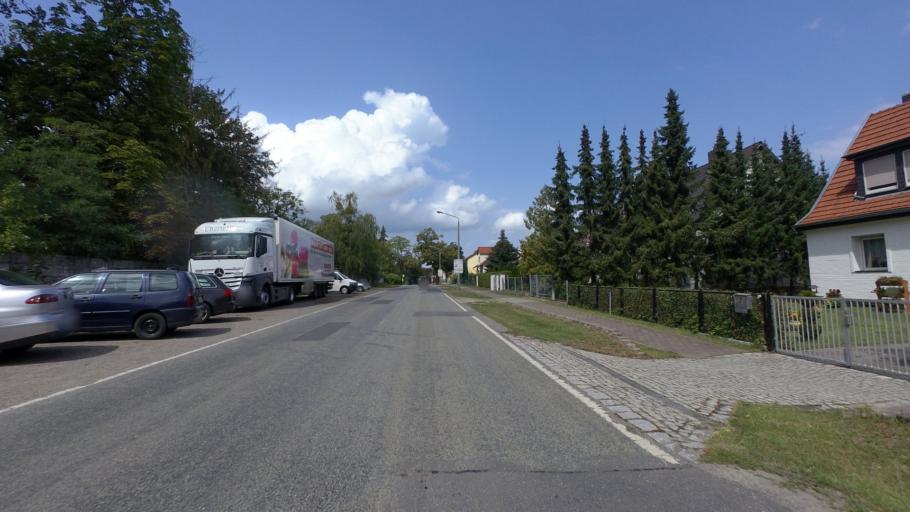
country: DE
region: Brandenburg
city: Teupitz
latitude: 52.1308
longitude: 13.6229
